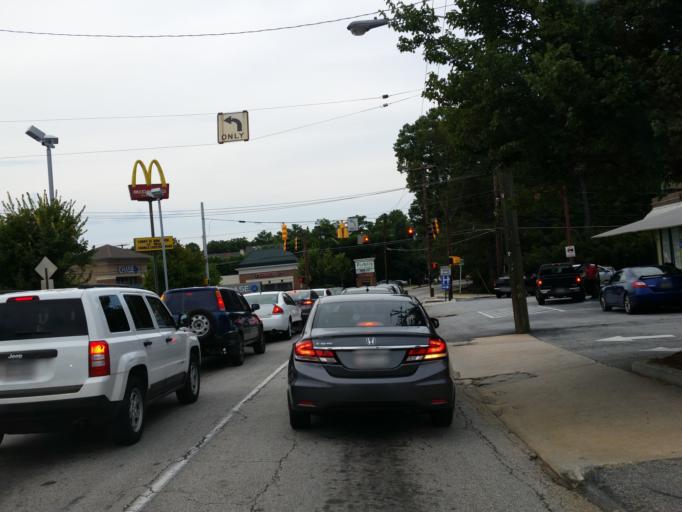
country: US
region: Georgia
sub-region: Fulton County
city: Atlanta
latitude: 33.8089
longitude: -84.4128
